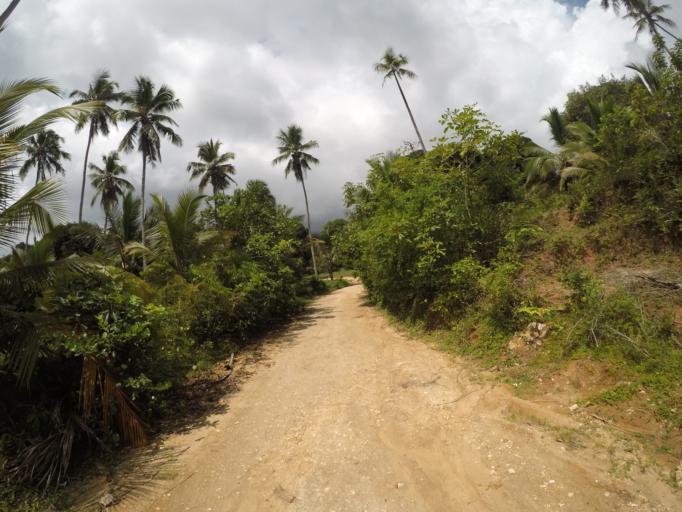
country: TZ
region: Pemba South
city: Mtambile
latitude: -5.3868
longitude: 39.7424
